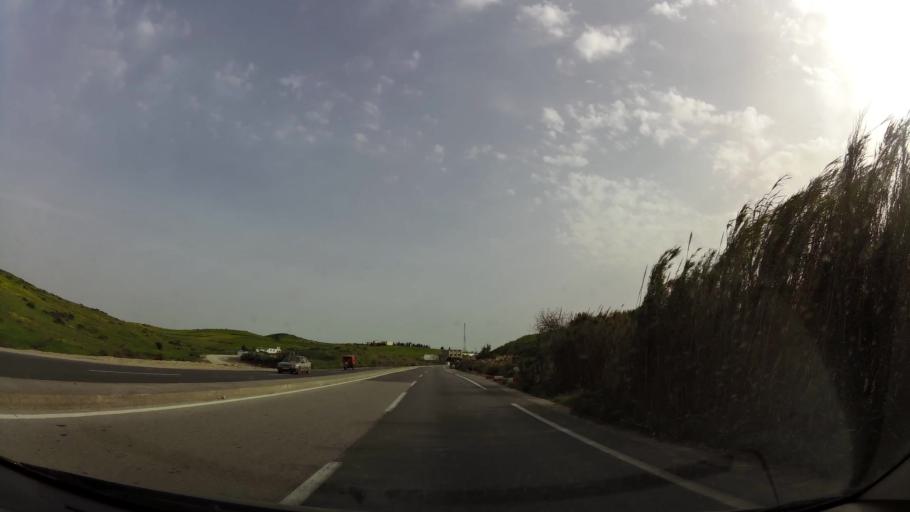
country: MA
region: Tanger-Tetouan
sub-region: Tanger-Assilah
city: Dar Chaoui
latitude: 35.6684
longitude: -5.6977
